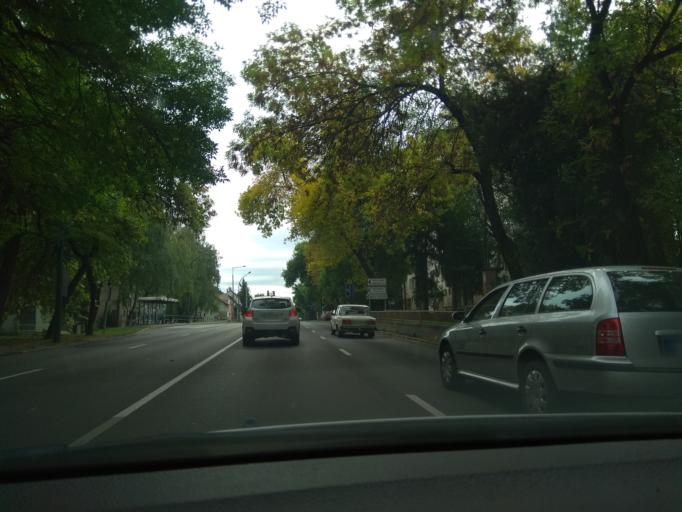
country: HU
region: Heves
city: Eger
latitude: 47.8844
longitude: 20.3811
